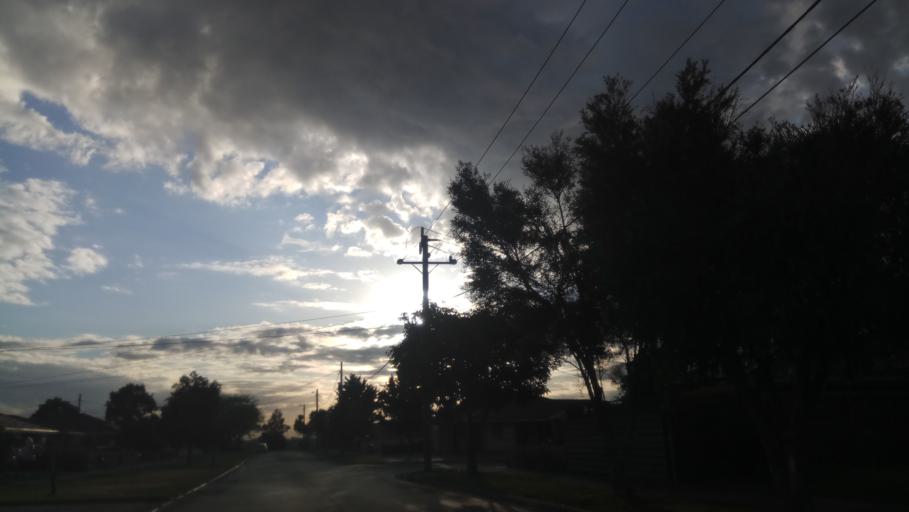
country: AU
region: Victoria
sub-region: Hobsons Bay
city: Altona Meadows
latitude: -37.8661
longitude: 144.7887
